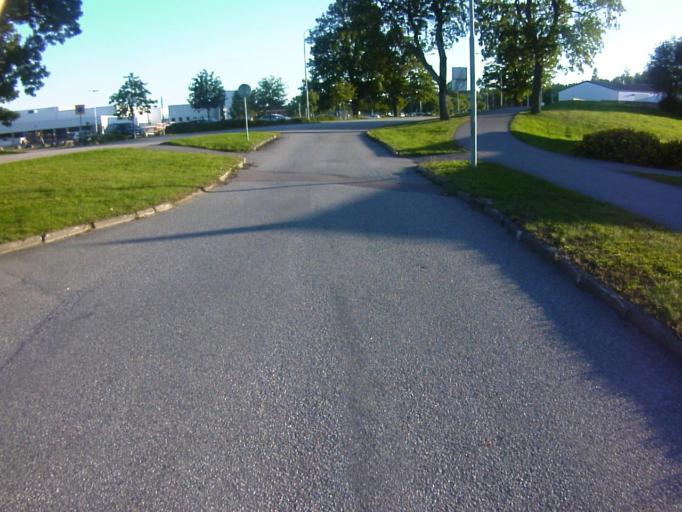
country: SE
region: Soedermanland
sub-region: Eskilstuna Kommun
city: Torshalla
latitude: 59.4010
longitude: 16.4486
